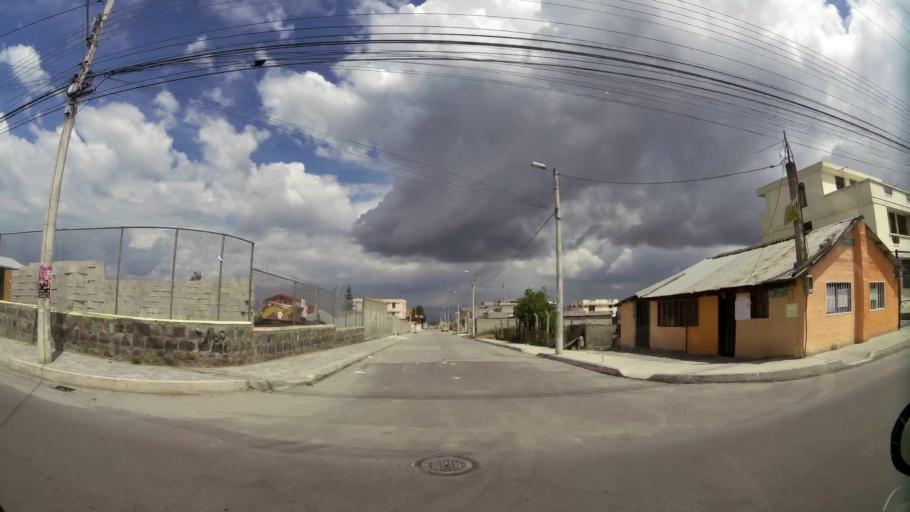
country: EC
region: Pichincha
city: Quito
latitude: -0.0641
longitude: -78.4169
